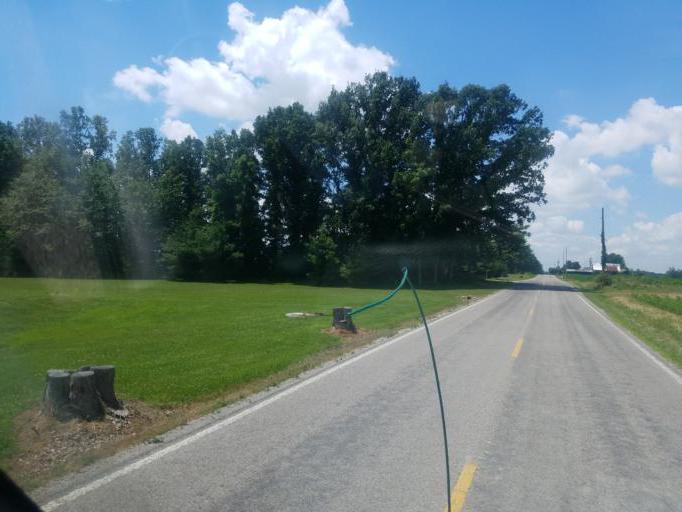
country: US
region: Ohio
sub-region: Huron County
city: Plymouth
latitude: 41.0680
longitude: -82.6342
